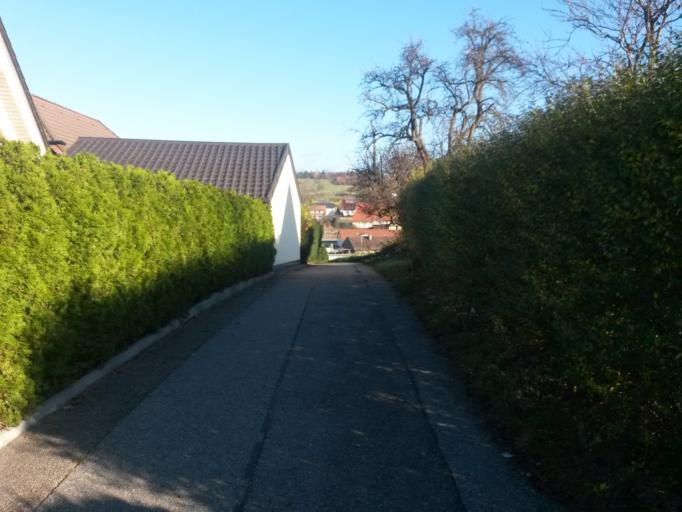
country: DE
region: Baden-Wuerttemberg
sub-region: Karlsruhe Region
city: Neuenburg
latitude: 48.8687
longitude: 8.5879
